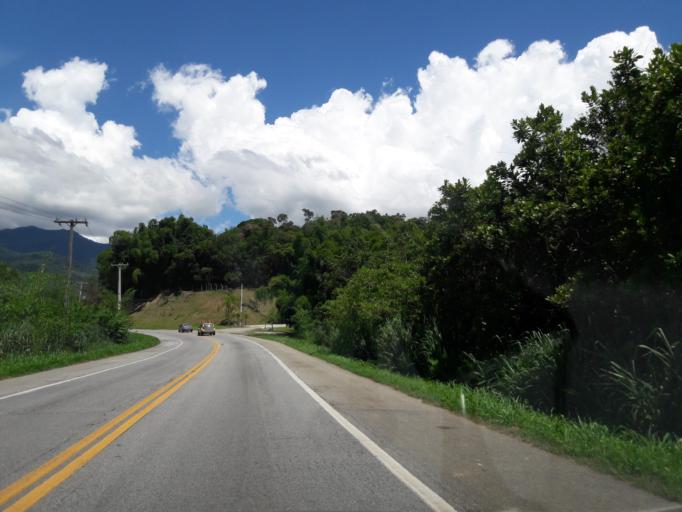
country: BR
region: Parana
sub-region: Antonina
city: Antonina
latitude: -25.5409
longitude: -48.7943
